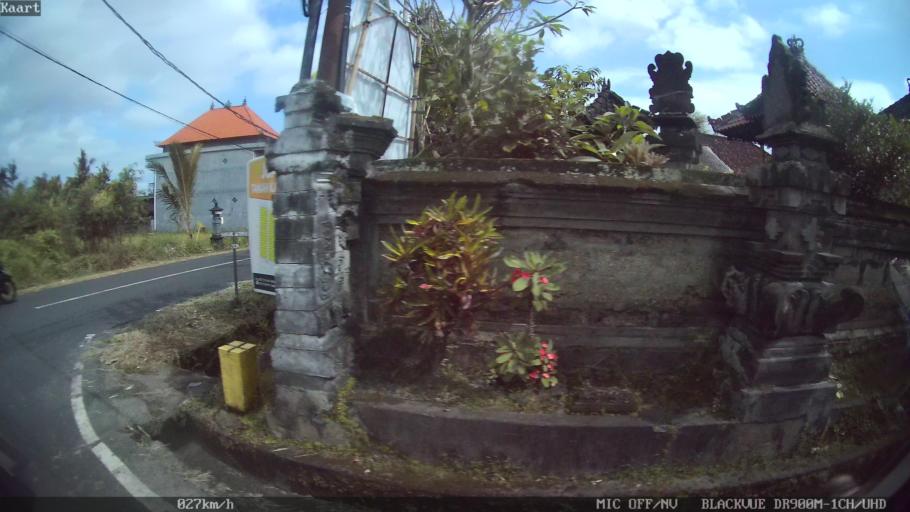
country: ID
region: Bali
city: Banjar Pesalakan
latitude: -8.5213
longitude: 115.3114
